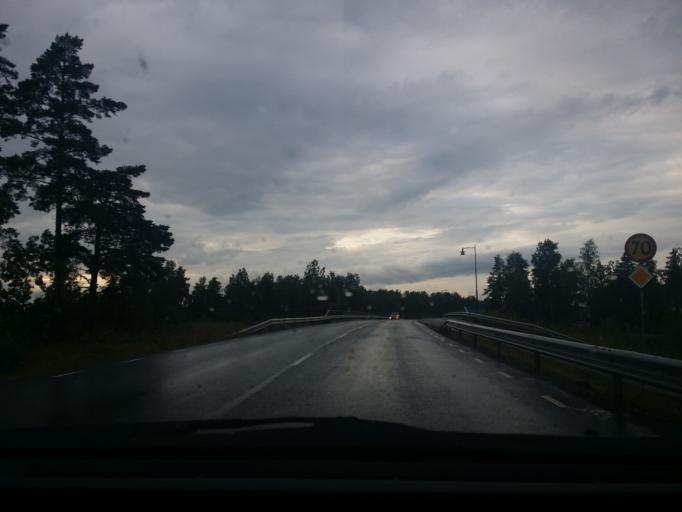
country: SE
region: Vaestmanland
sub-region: Arboga Kommun
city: Arboga
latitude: 59.4239
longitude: 15.8258
